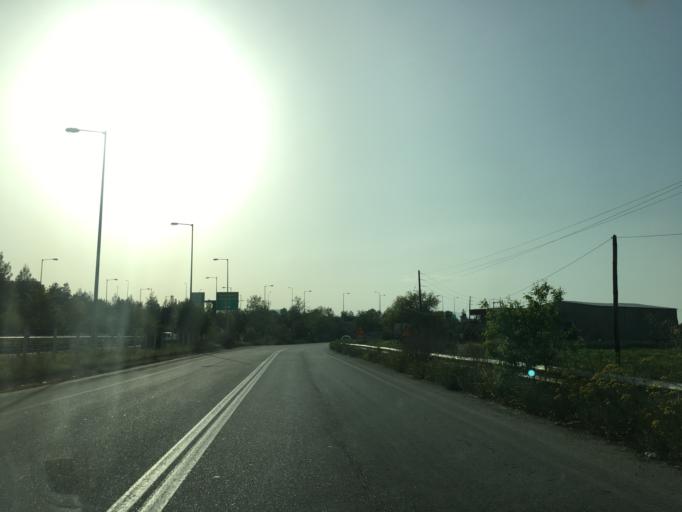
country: GR
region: Thessaly
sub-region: Nomos Magnisias
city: Velestino
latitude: 39.3889
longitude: 22.7689
